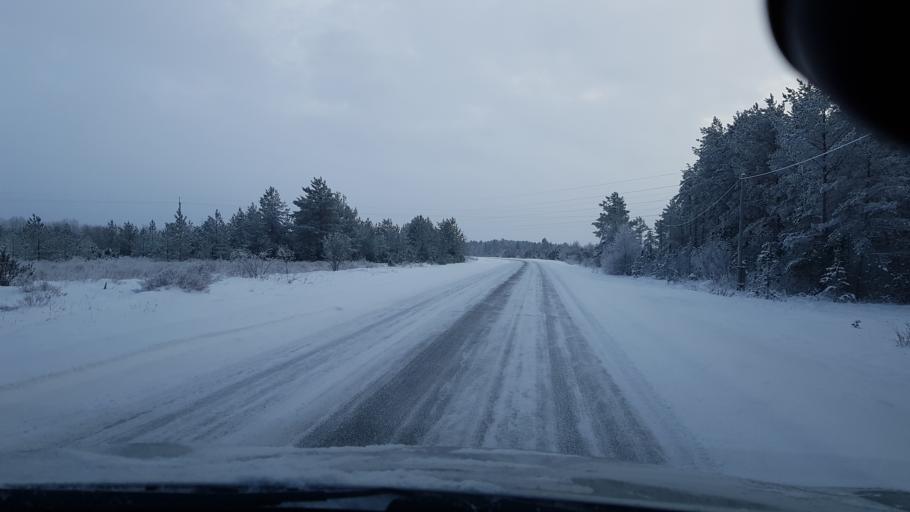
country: EE
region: Harju
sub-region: Keila linn
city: Keila
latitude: 59.3519
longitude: 24.4273
